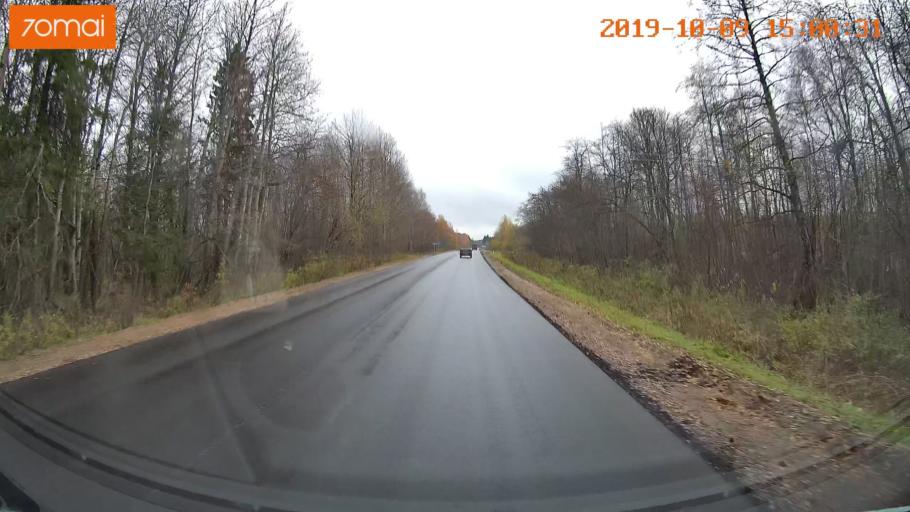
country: RU
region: Kostroma
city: Chistyye Bory
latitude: 58.3083
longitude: 41.6783
